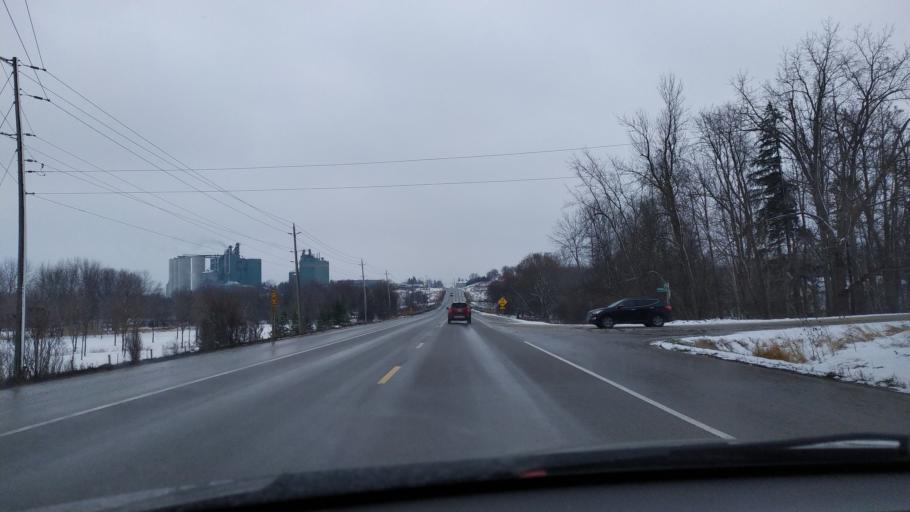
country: CA
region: Ontario
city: Waterloo
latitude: 43.6040
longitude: -80.6454
